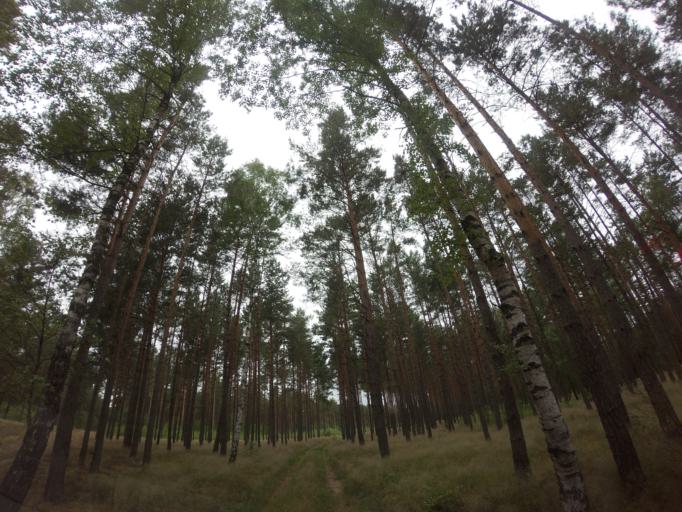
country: PL
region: West Pomeranian Voivodeship
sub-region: Powiat choszczenski
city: Drawno
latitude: 53.1430
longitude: 15.7136
